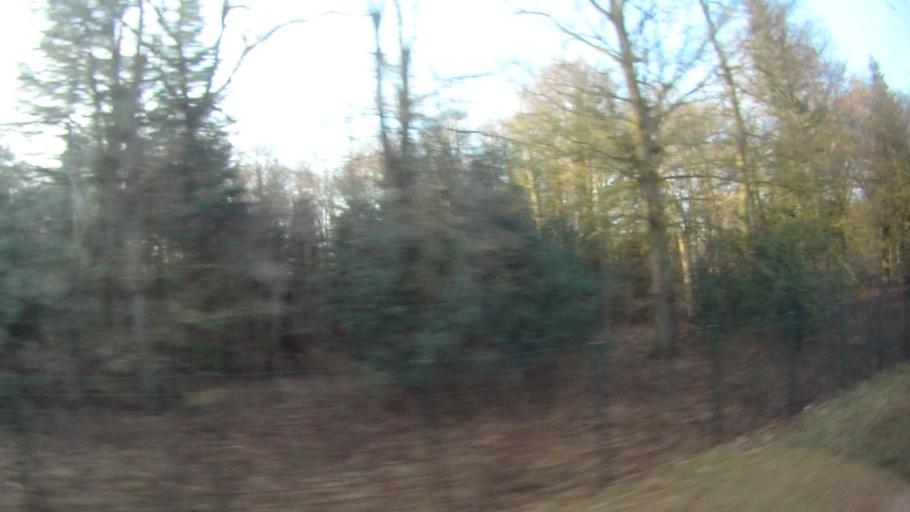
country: NL
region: Gelderland
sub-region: Gemeente Ermelo
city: Ermelo
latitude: 52.3037
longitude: 5.6160
